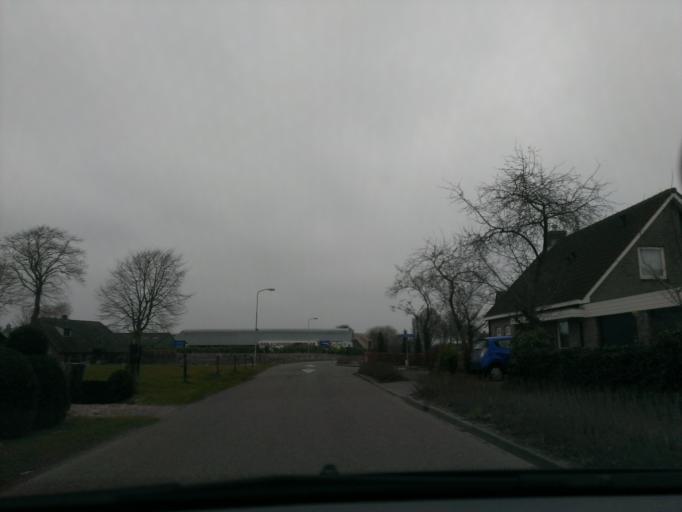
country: NL
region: Gelderland
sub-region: Gemeente Heerde
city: Heerde
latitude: 52.3907
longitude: 6.0239
